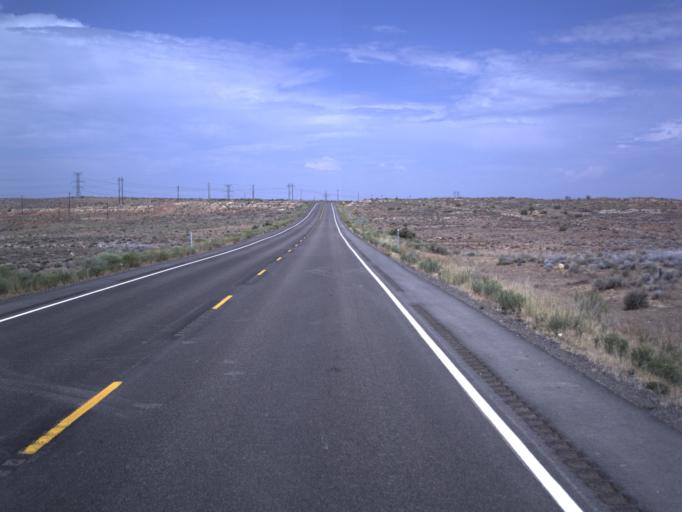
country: US
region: Utah
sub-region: Uintah County
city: Naples
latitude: 40.2110
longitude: -109.3732
